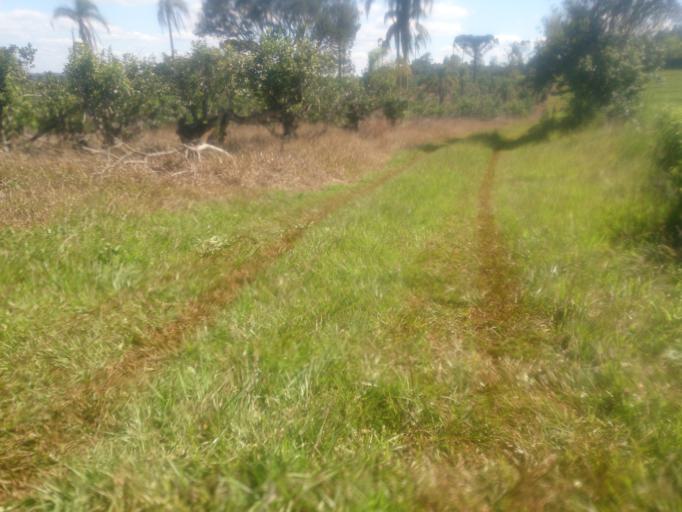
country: AR
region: Misiones
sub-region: Departamento de Obera
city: Obera
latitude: -27.4380
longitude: -55.1130
